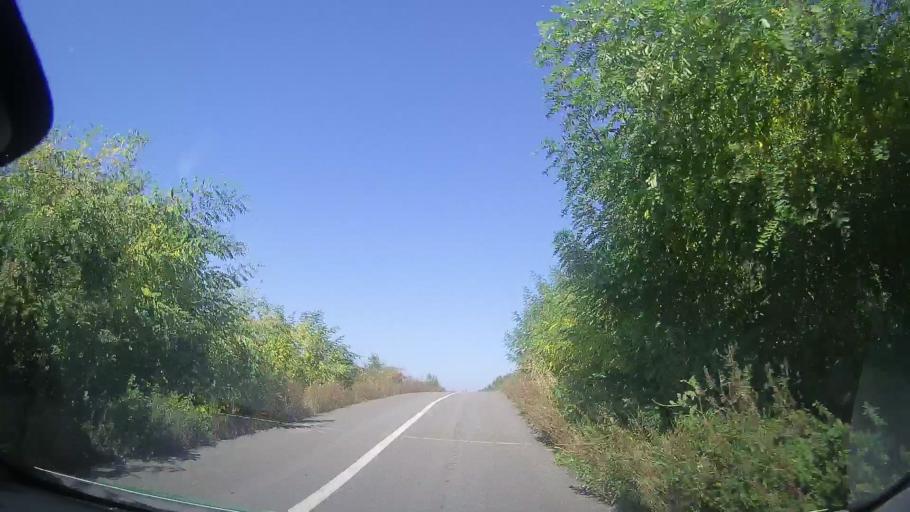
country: RO
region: Timis
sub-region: Comuna Bara
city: Bara
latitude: 45.8830
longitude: 21.8855
